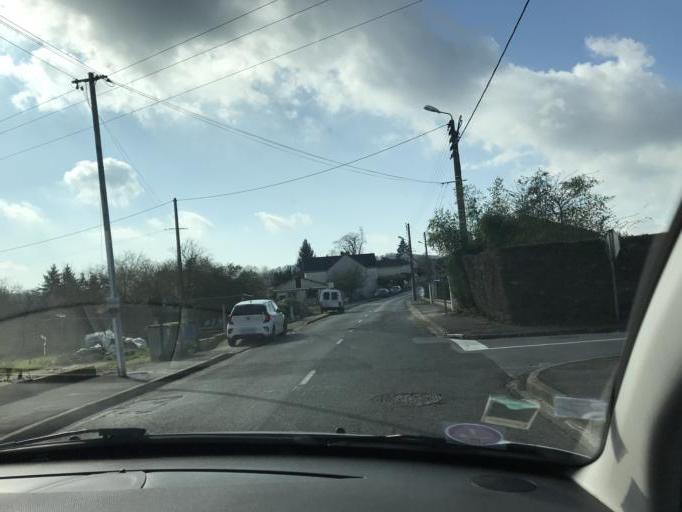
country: FR
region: Picardie
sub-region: Departement de l'Aisne
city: Billy-sur-Aisne
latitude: 49.3612
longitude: 3.3882
